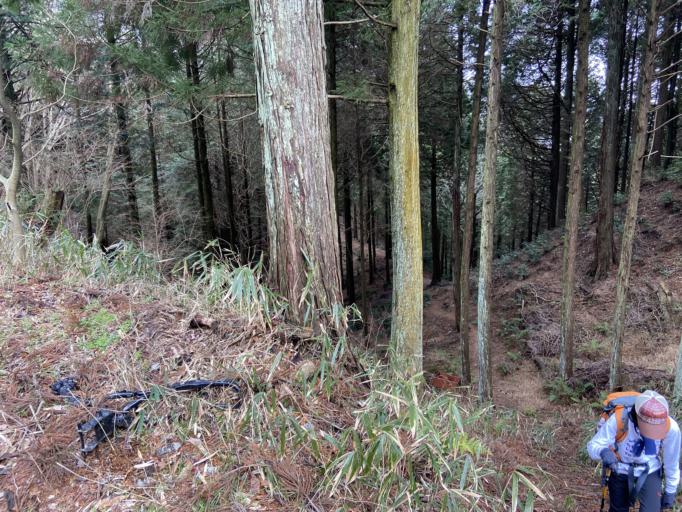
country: JP
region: Hyogo
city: Kobe
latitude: 34.7466
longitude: 135.1891
